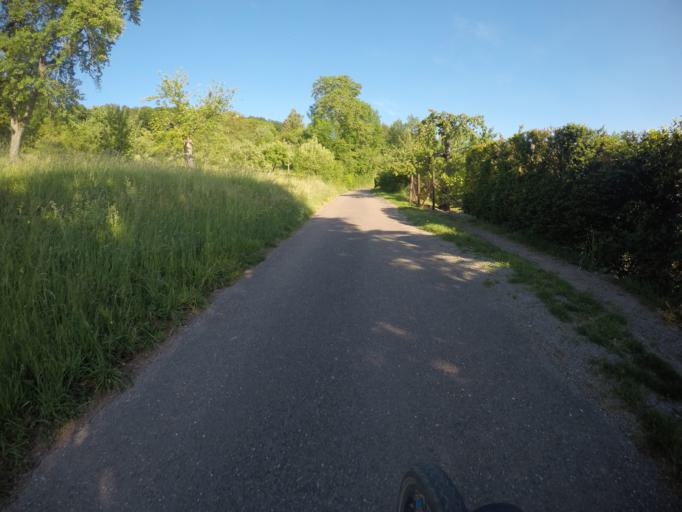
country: DE
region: Baden-Wuerttemberg
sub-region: Regierungsbezirk Stuttgart
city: Esslingen
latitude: 48.7606
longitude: 9.3213
